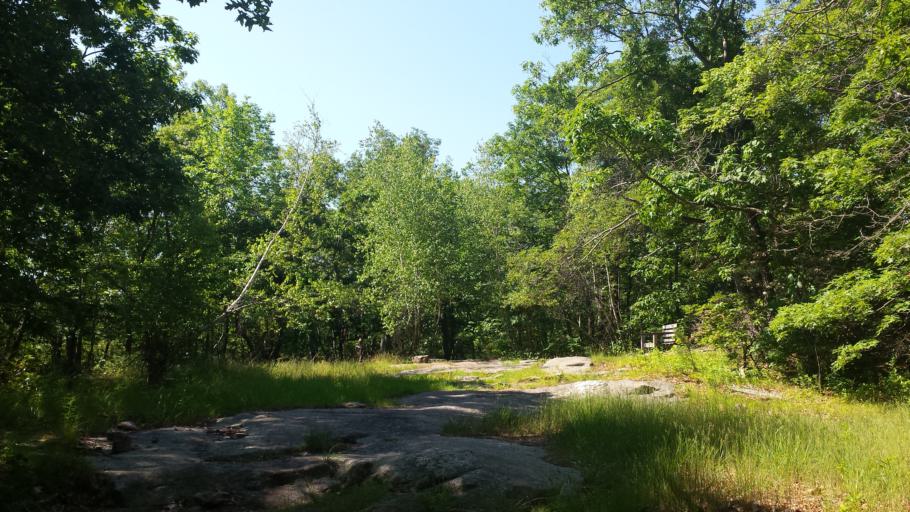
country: US
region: New York
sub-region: Westchester County
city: Pound Ridge
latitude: 41.2453
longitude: -73.5732
